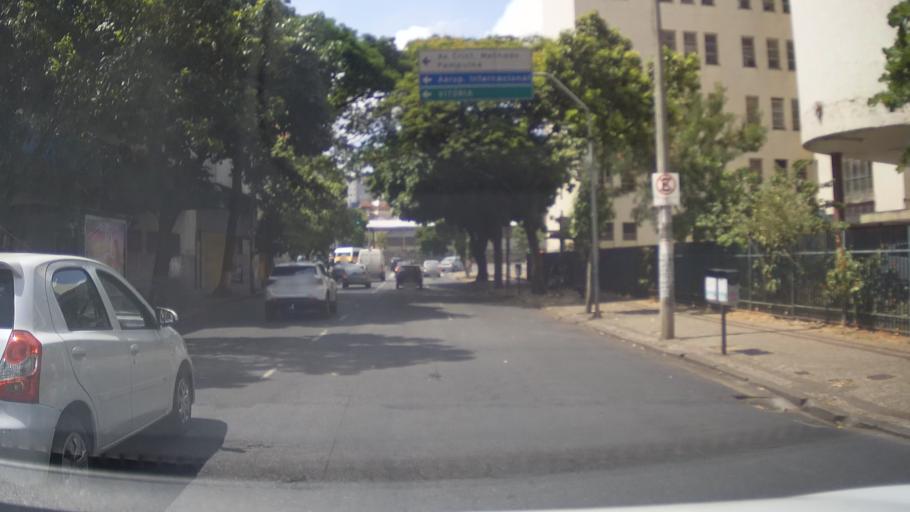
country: BR
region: Minas Gerais
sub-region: Belo Horizonte
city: Belo Horizonte
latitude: -19.9154
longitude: -43.9363
